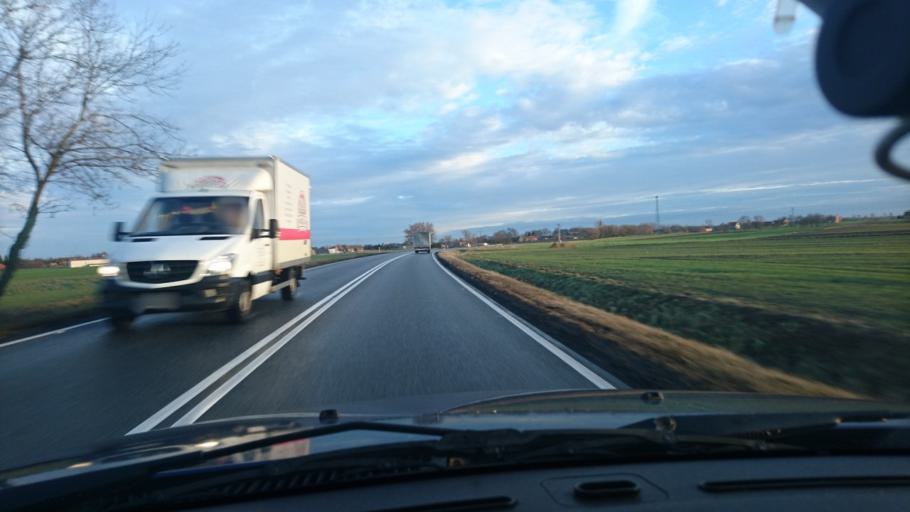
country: PL
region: Greater Poland Voivodeship
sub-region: Powiat kepinski
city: Opatow
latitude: 51.2204
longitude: 18.1344
